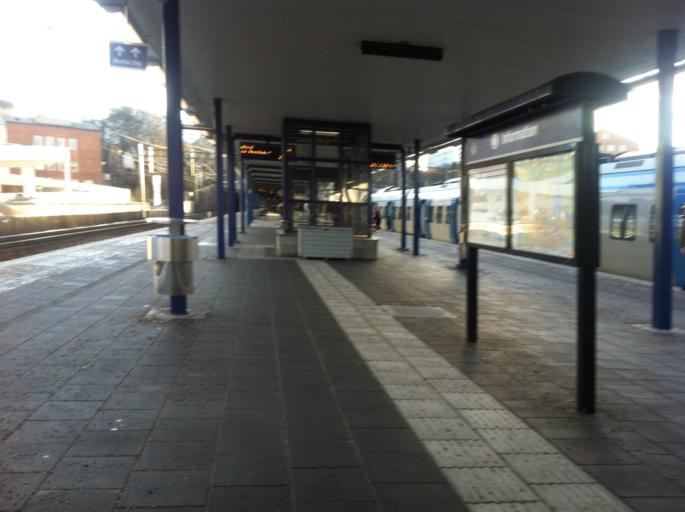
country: SE
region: Stockholm
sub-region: Solna Kommun
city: Solna
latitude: 59.3671
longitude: 18.0095
